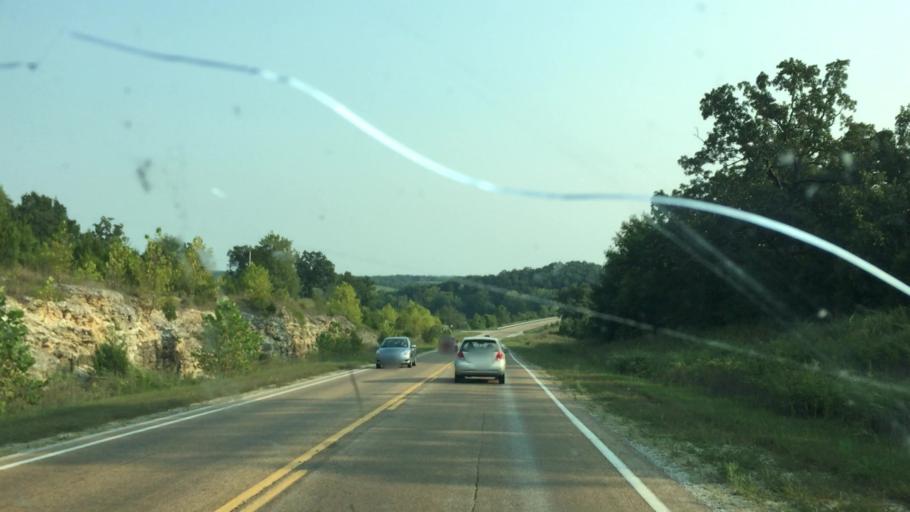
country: US
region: Missouri
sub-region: Pulaski County
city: Richland
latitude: 37.8072
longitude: -92.4058
